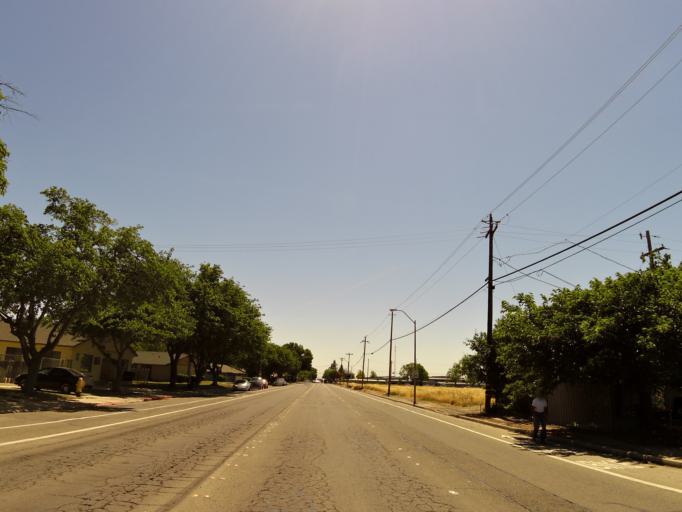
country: US
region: California
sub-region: Merced County
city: Merced
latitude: 37.2940
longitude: -120.5057
